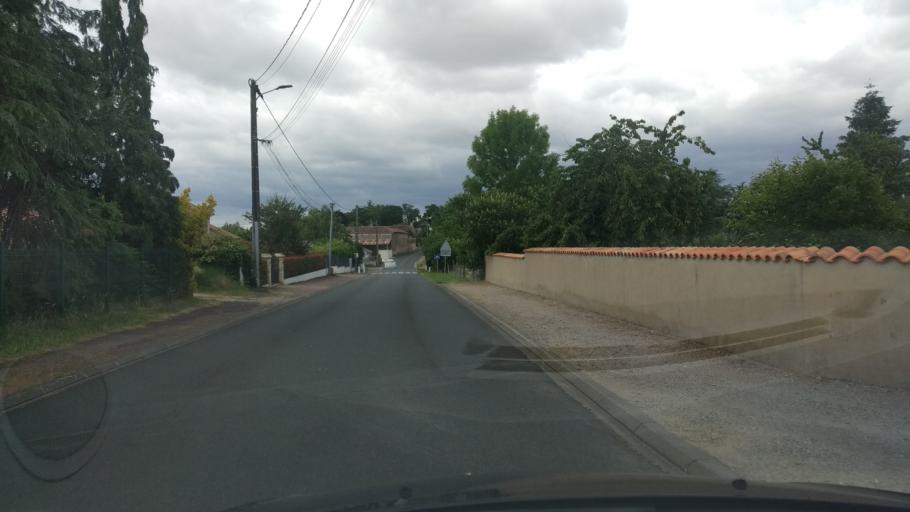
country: FR
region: Poitou-Charentes
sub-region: Departement de la Vienne
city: Vouille
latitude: 46.6296
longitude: 0.1878
